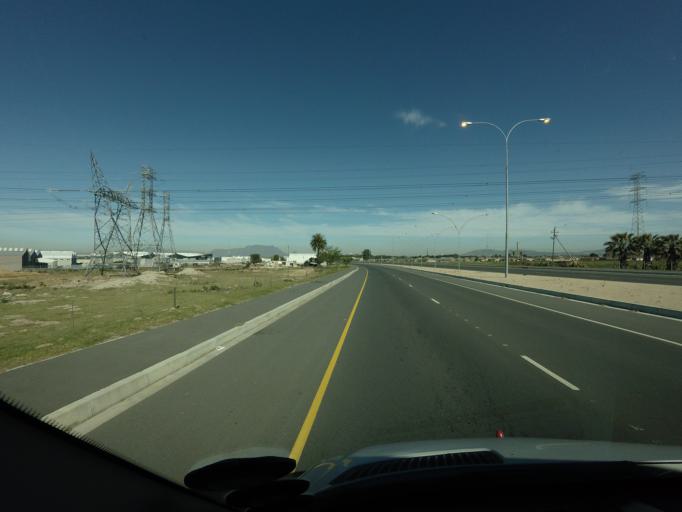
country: ZA
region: Western Cape
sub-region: City of Cape Town
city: Kraaifontein
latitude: -33.9502
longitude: 18.7069
